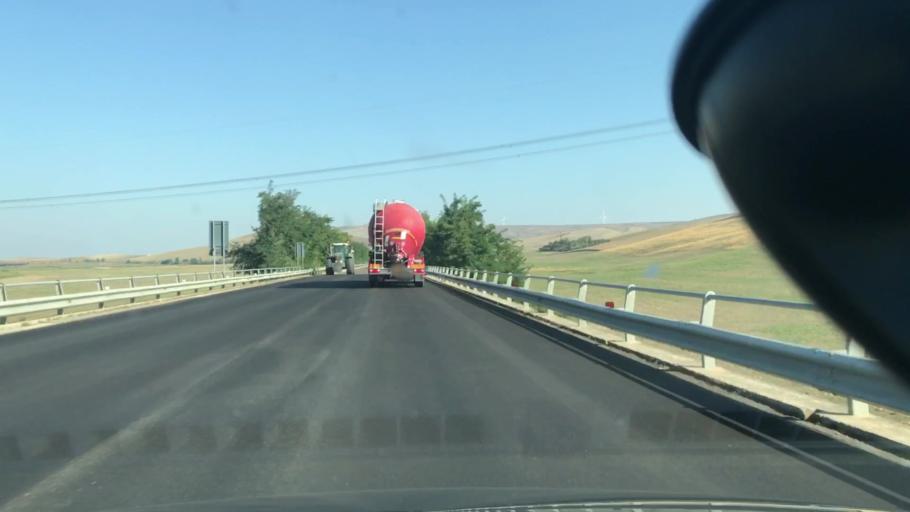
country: IT
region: Basilicate
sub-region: Provincia di Matera
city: Irsina
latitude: 40.7988
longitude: 16.2749
